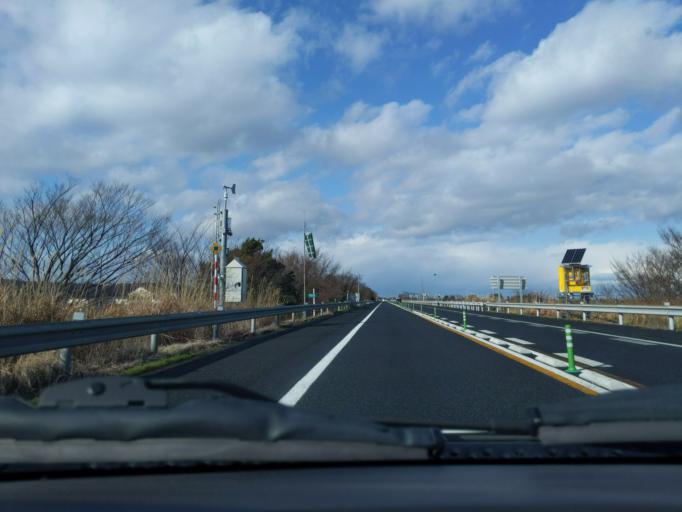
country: JP
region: Niigata
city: Gosen
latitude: 37.7802
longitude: 139.1743
